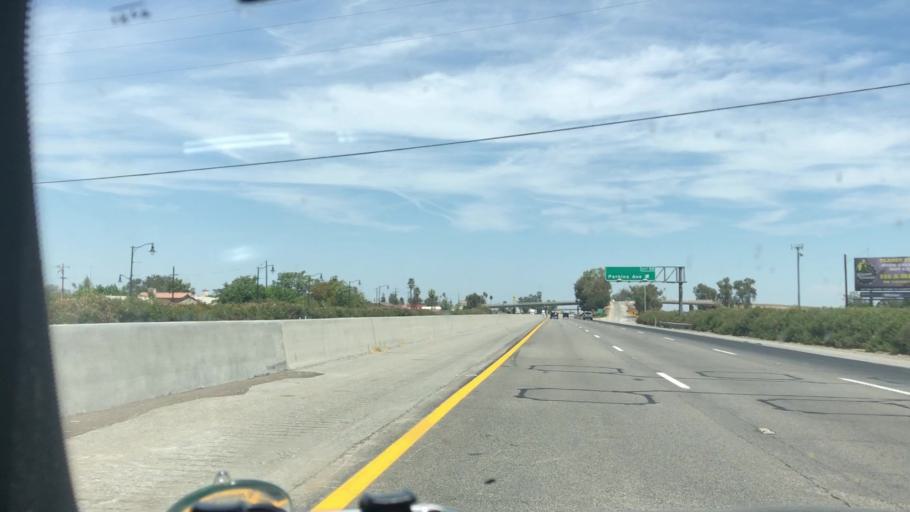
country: US
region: California
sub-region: Kern County
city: McFarland
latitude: 35.6784
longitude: -119.2275
